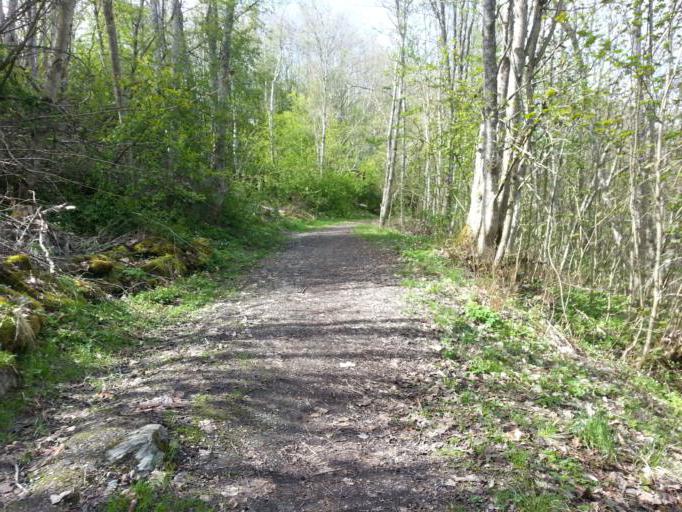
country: NO
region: Sor-Trondelag
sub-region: Trondheim
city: Trondheim
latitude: 63.3875
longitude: 10.3602
